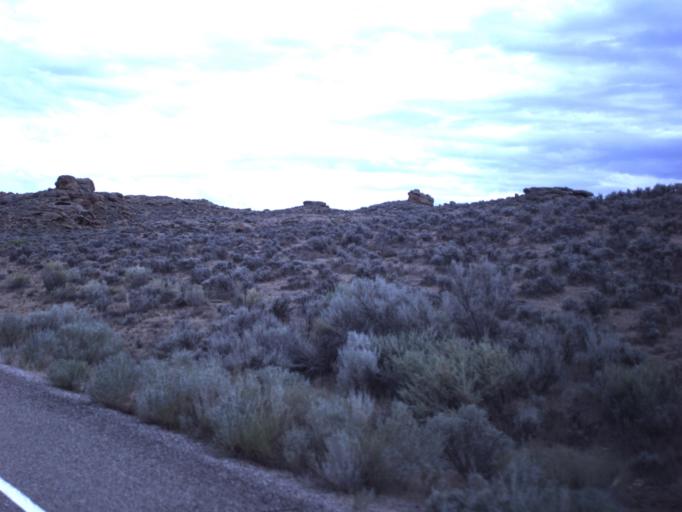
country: US
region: Colorado
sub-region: Rio Blanco County
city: Rangely
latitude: 39.9701
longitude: -109.1694
